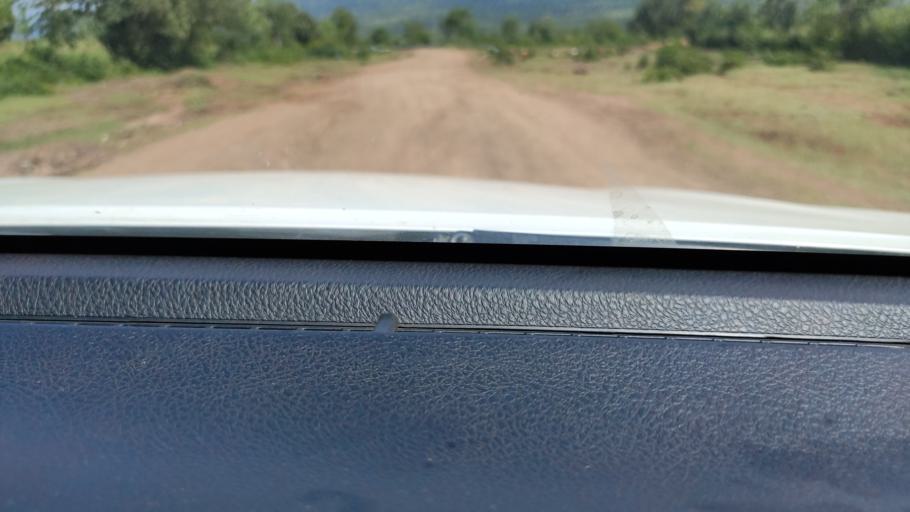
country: ET
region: Southern Nations, Nationalities, and People's Region
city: Felege Neway
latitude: 6.3657
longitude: 36.9827
